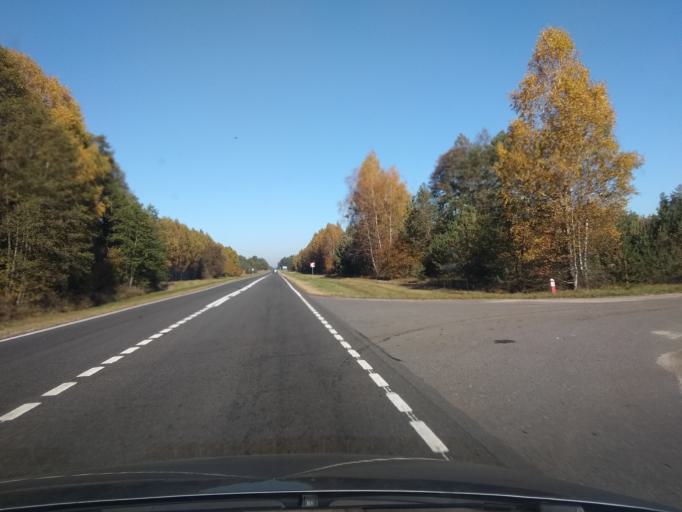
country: BY
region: Brest
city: Kobryn
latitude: 52.0670
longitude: 24.2842
